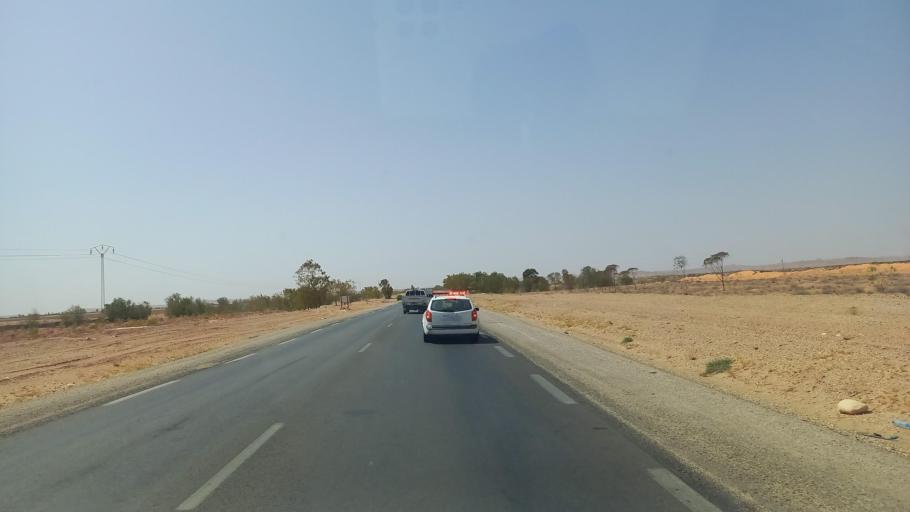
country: TN
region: Madanin
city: Medenine
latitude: 33.2243
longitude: 10.4510
